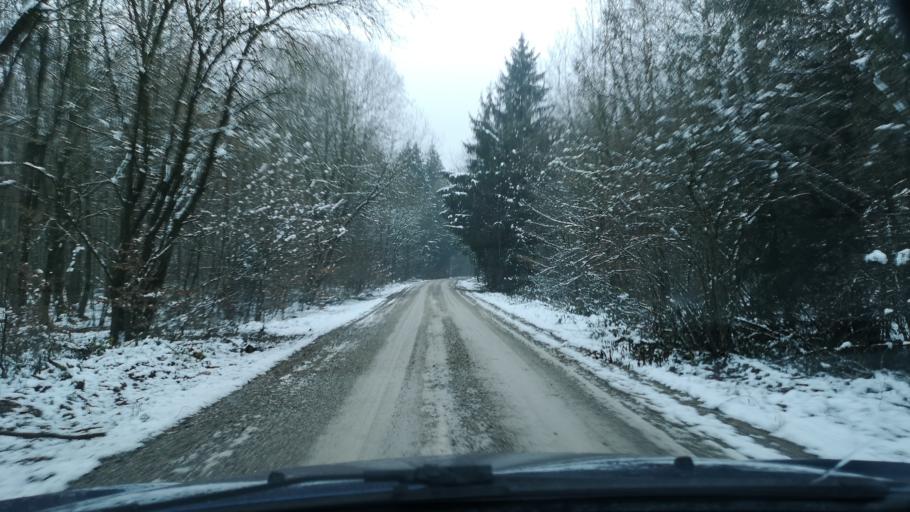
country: DE
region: Bavaria
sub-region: Upper Bavaria
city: Anzing
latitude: 48.1362
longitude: 11.8727
